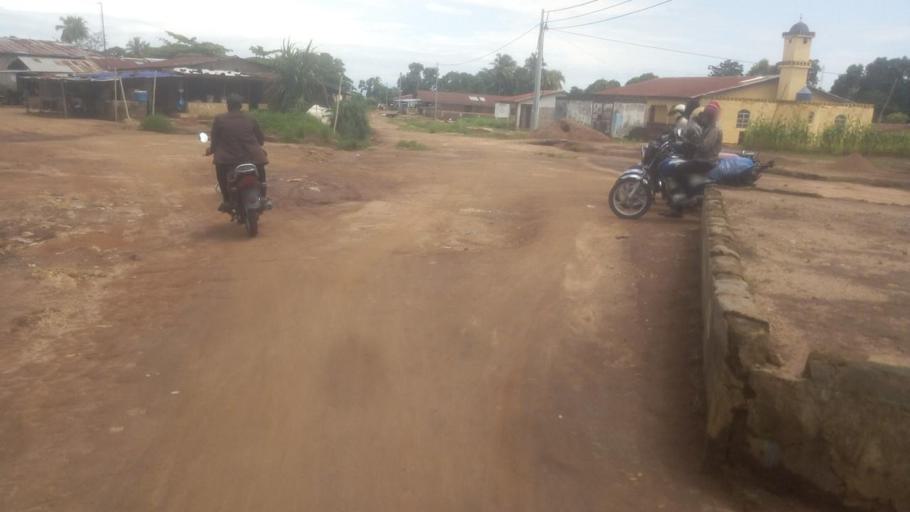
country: SL
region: Northern Province
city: Masoyila
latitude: 8.6022
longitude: -13.2004
